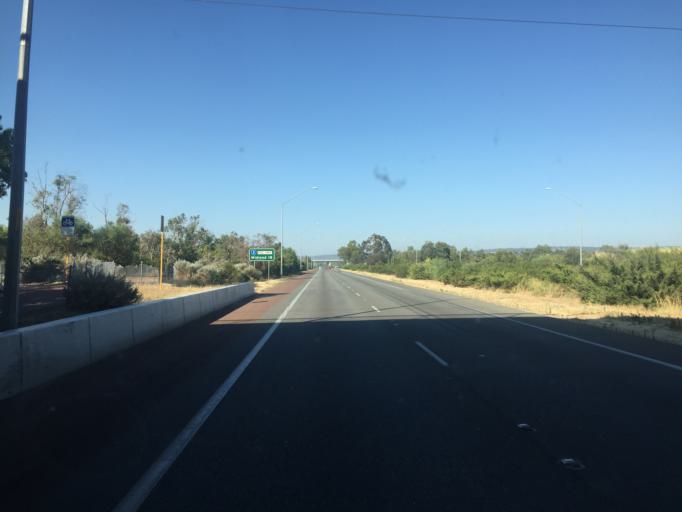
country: AU
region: Western Australia
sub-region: Gosnells
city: Kenwick
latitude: -32.0323
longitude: 115.9652
